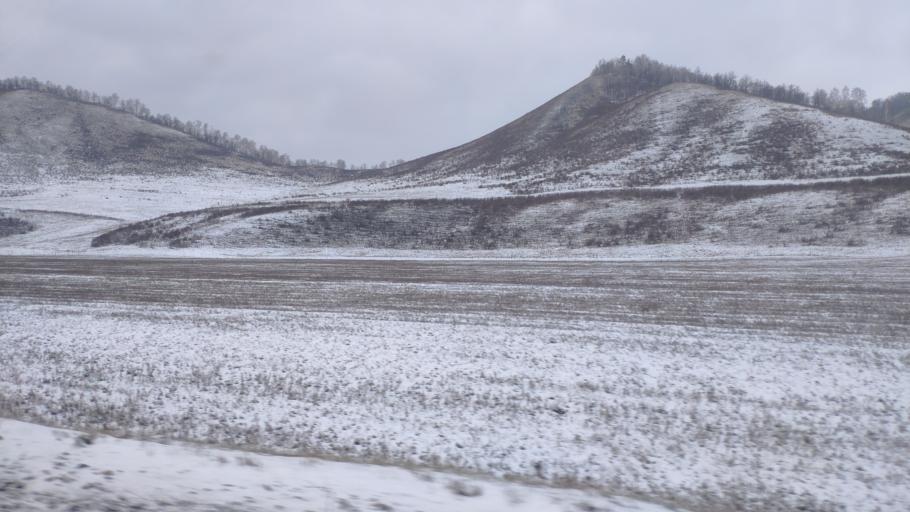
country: RU
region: Bashkortostan
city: Isyangulovo
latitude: 52.1612
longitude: 56.8976
